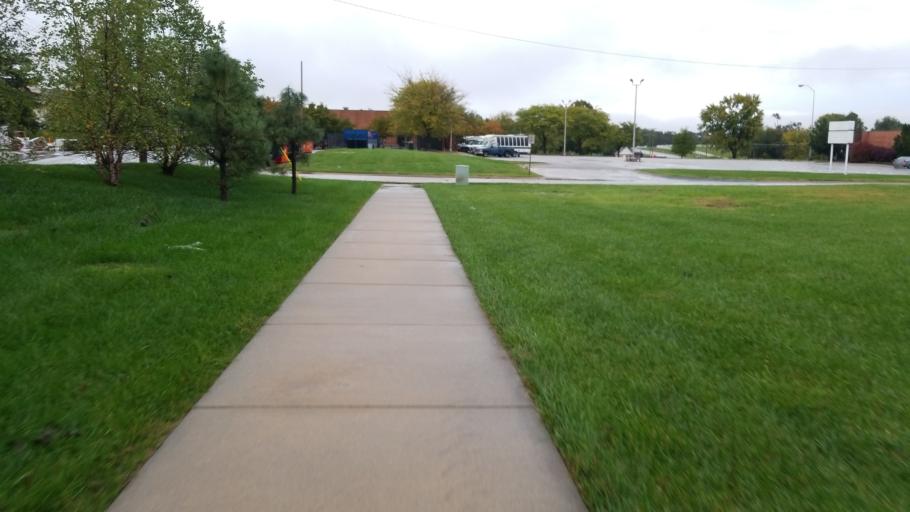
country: US
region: Nebraska
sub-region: Sarpy County
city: Offutt Air Force Base
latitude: 41.1264
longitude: -95.9489
